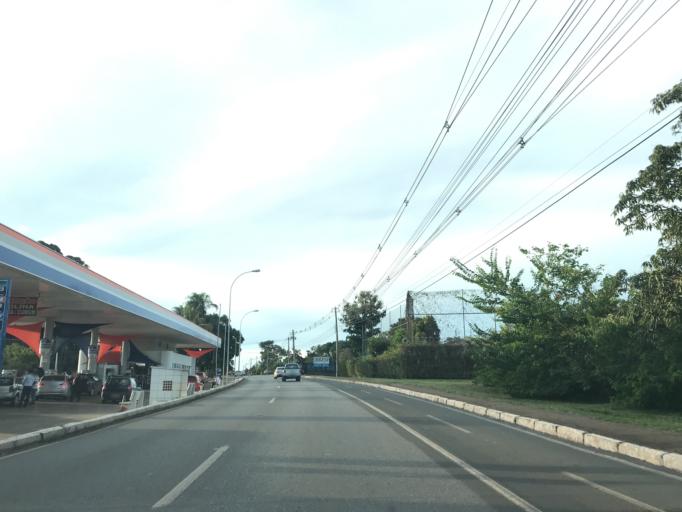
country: BR
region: Federal District
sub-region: Brasilia
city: Brasilia
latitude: -15.8212
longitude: -47.8049
